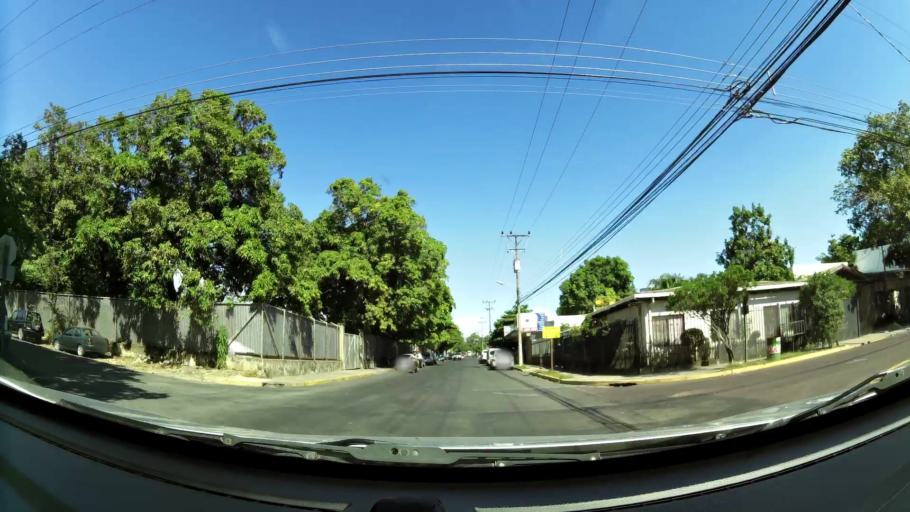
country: CR
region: Guanacaste
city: Liberia
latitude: 10.6331
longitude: -85.4422
